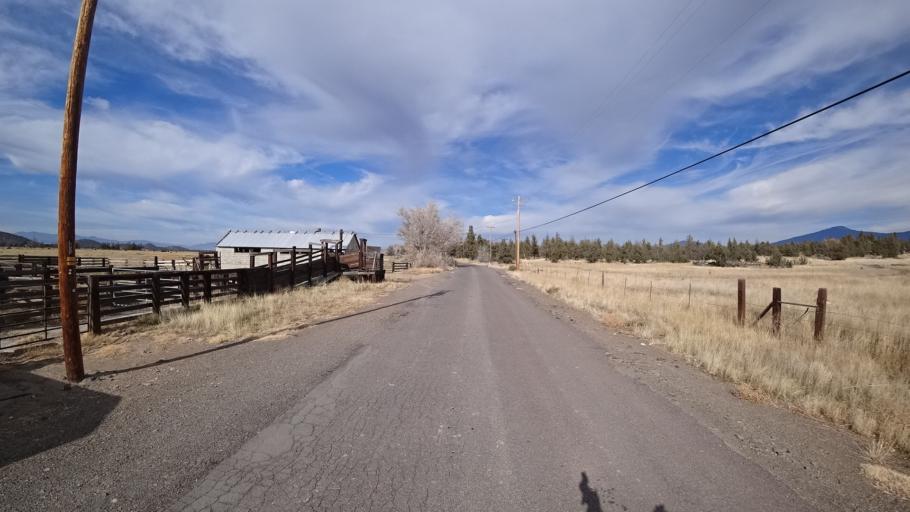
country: US
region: California
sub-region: Siskiyou County
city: Weed
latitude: 41.5998
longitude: -122.4034
